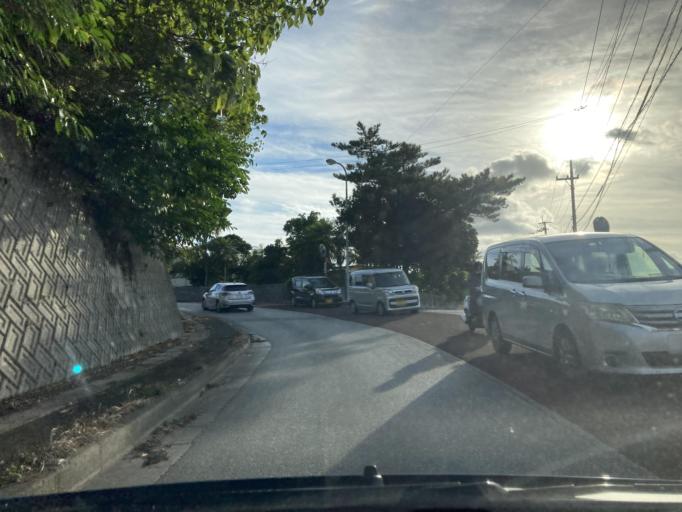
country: JP
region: Okinawa
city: Tomigusuku
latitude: 26.1594
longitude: 127.7373
